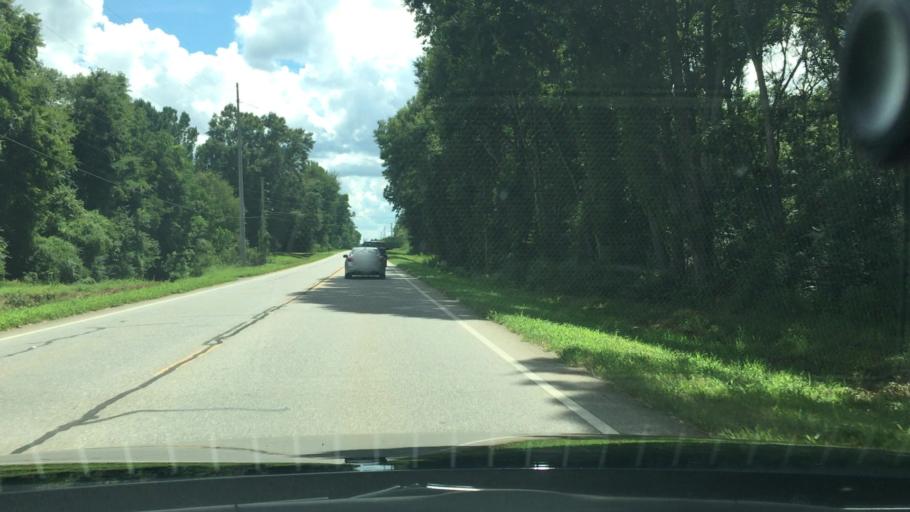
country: US
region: Georgia
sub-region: Putnam County
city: Eatonton
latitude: 33.3434
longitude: -83.3615
